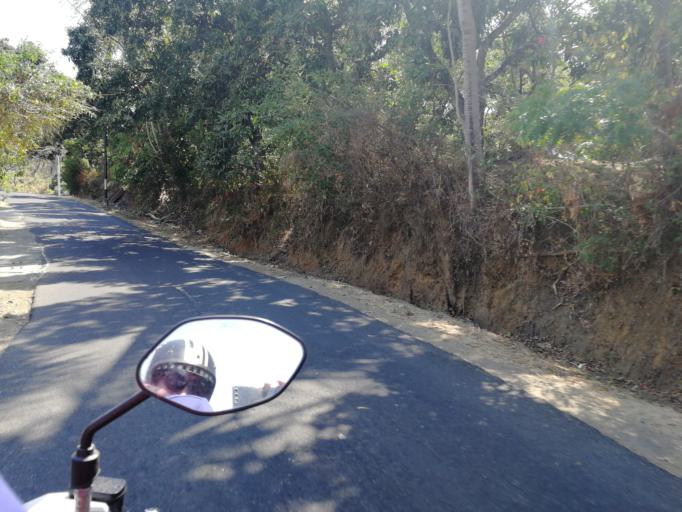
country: ID
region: Bali
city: Banjar Trunyan
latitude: -8.1276
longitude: 115.3258
